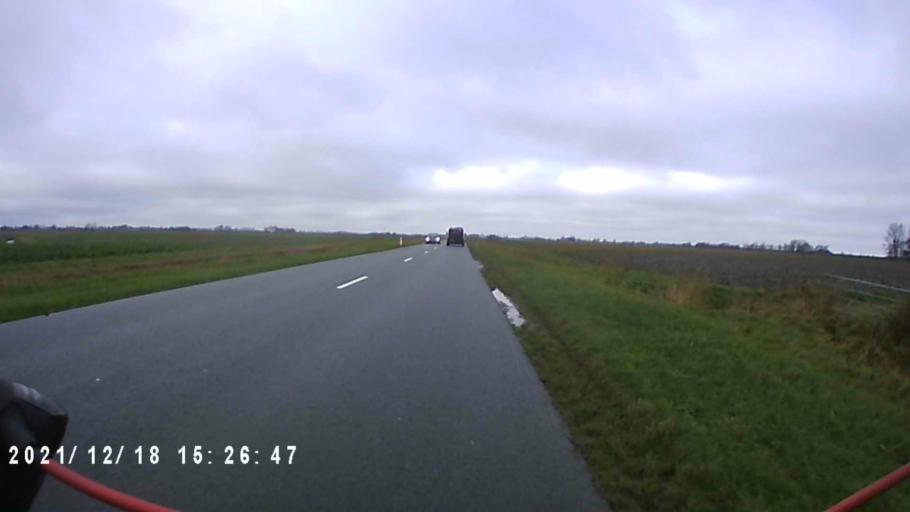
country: NL
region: Friesland
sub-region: Gemeente Kollumerland en Nieuwkruisland
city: Kollum
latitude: 53.3279
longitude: 6.1489
